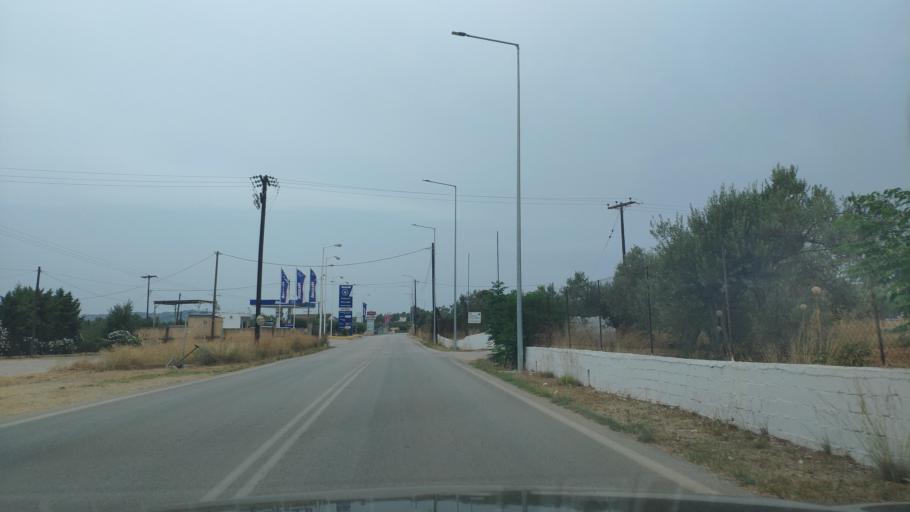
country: GR
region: Peloponnese
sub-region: Nomos Argolidos
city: Porto Cheli
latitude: 37.3449
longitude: 23.1575
